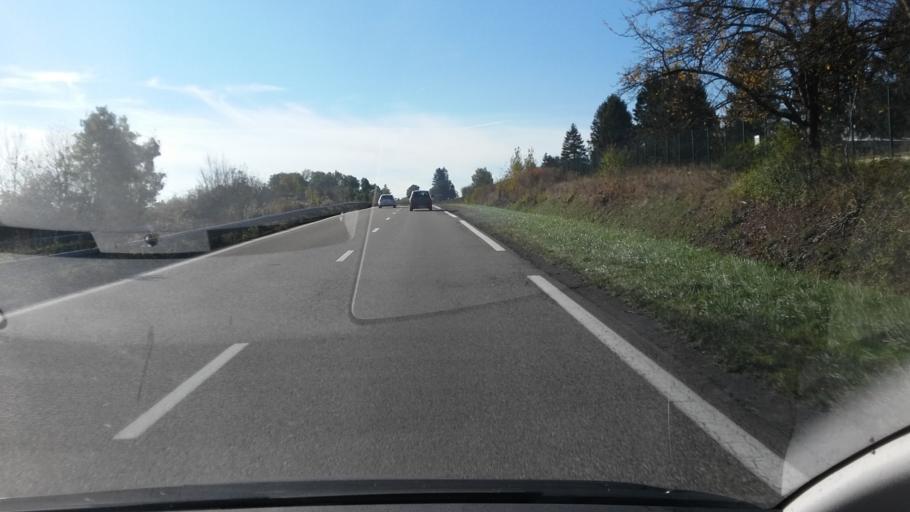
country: FR
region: Lorraine
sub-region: Departement de la Moselle
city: Phalsbourg
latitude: 48.7604
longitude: 7.2119
